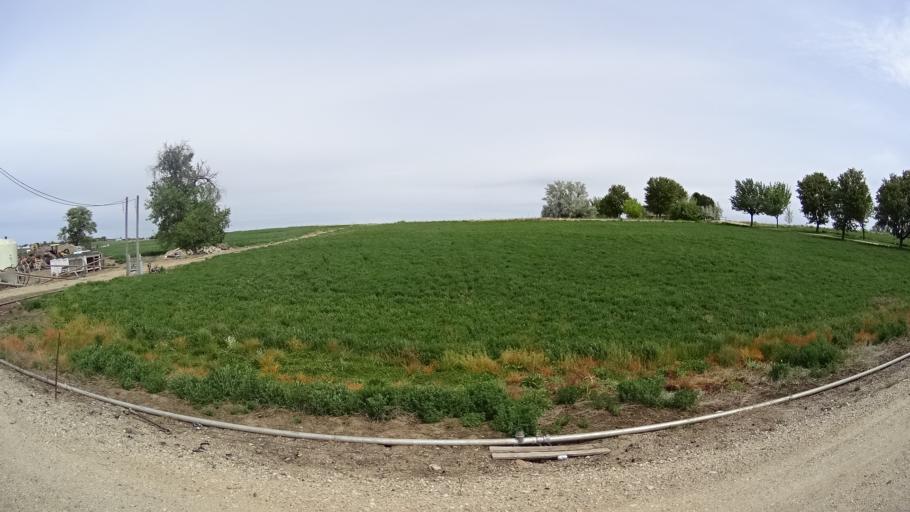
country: US
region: Idaho
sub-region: Ada County
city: Meridian
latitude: 43.5610
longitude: -116.4087
